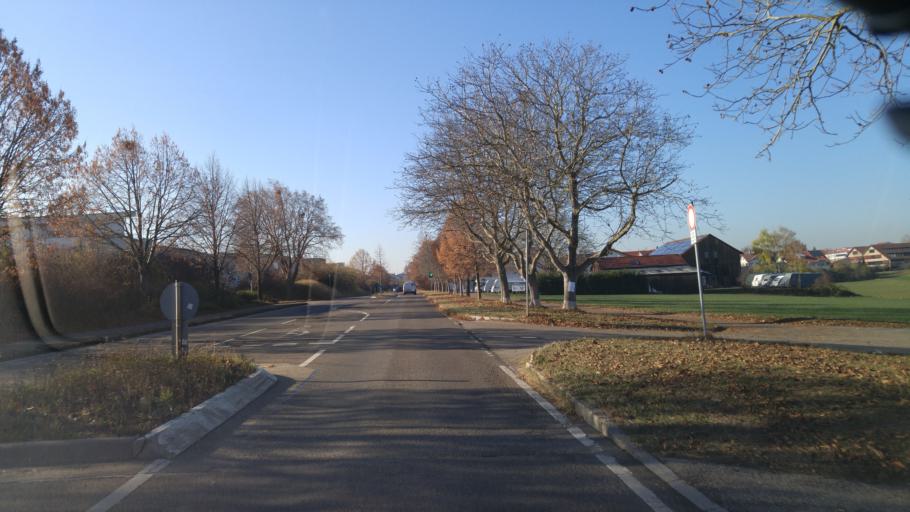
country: DE
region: Baden-Wuerttemberg
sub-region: Regierungsbezirk Stuttgart
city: Leonberg
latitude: 48.8177
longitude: 9.0325
